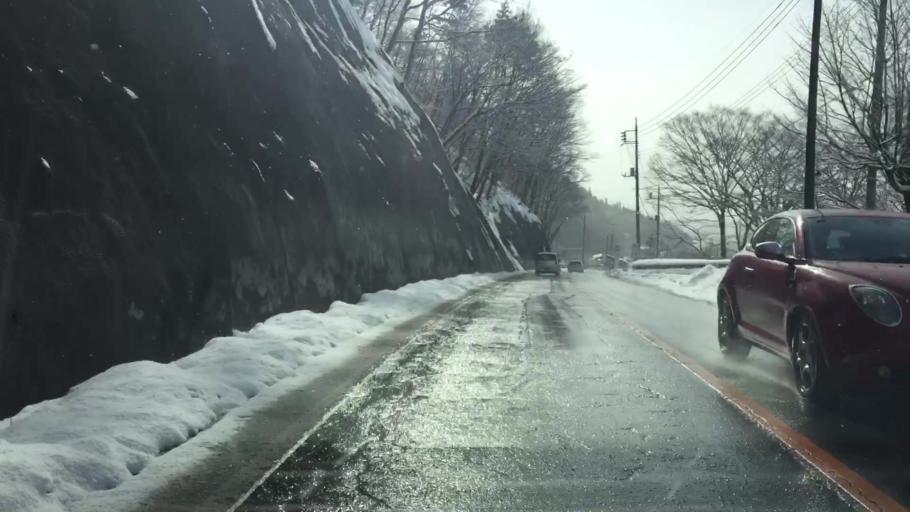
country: JP
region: Gunma
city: Numata
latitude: 36.6812
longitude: 139.0630
